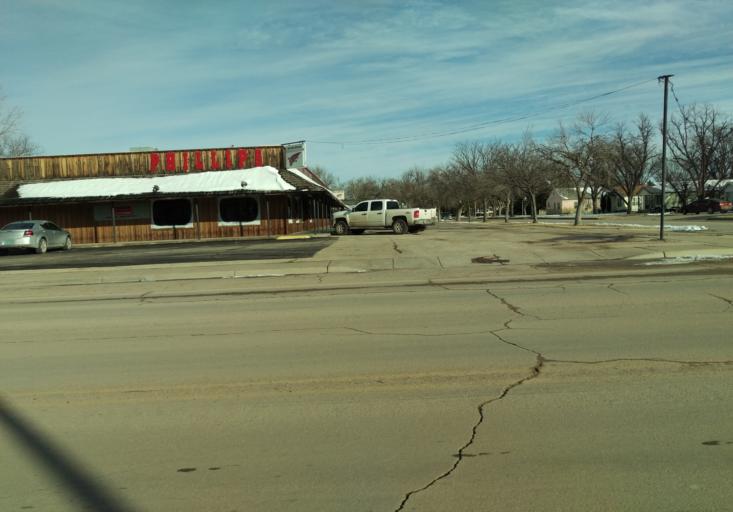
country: US
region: New Mexico
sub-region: Eddy County
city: Carlsbad
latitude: 32.4204
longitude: -104.2357
